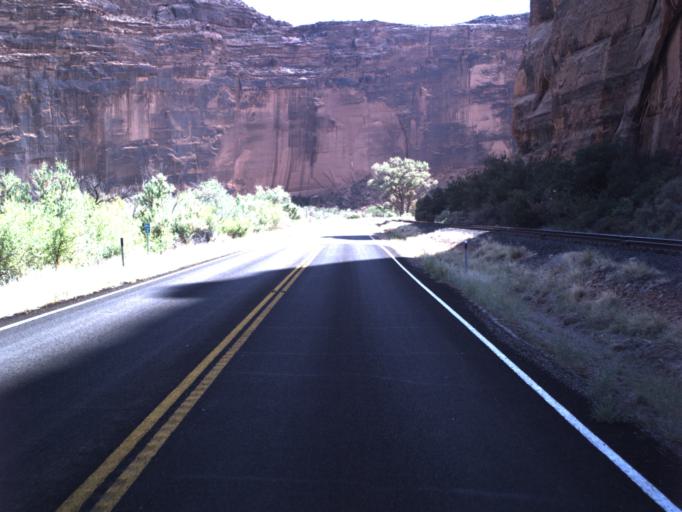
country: US
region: Utah
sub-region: Grand County
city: Moab
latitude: 38.5511
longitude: -109.6483
